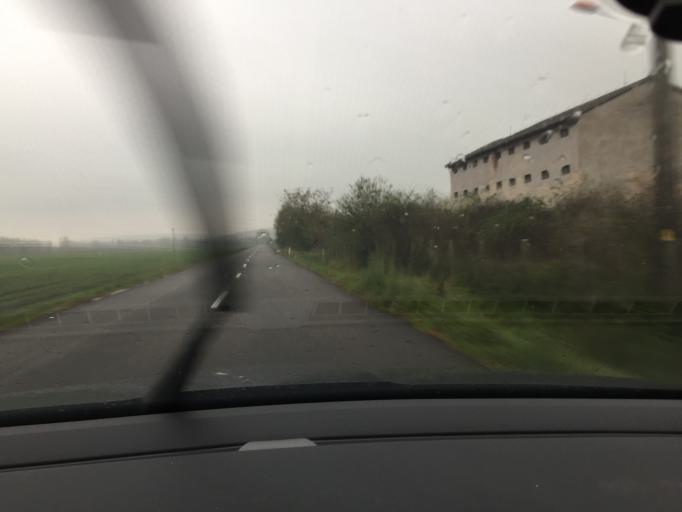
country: SK
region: Nitriansky
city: Zeliezovce
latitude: 47.9885
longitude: 18.7682
